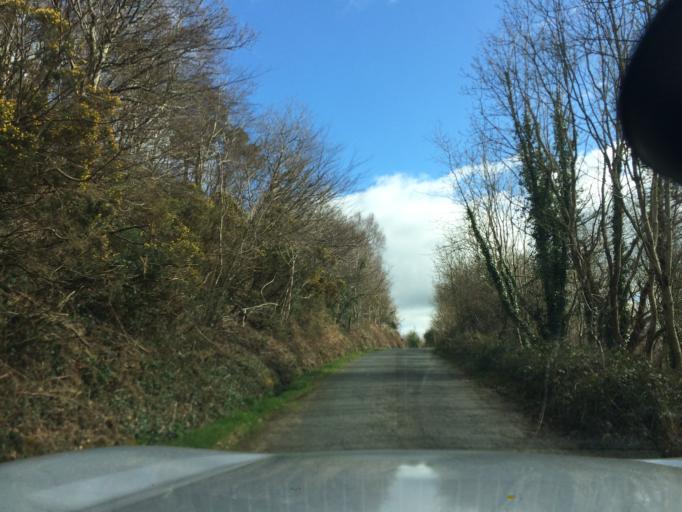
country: IE
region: Munster
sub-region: Waterford
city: Portlaw
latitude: 52.2794
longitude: -7.3701
